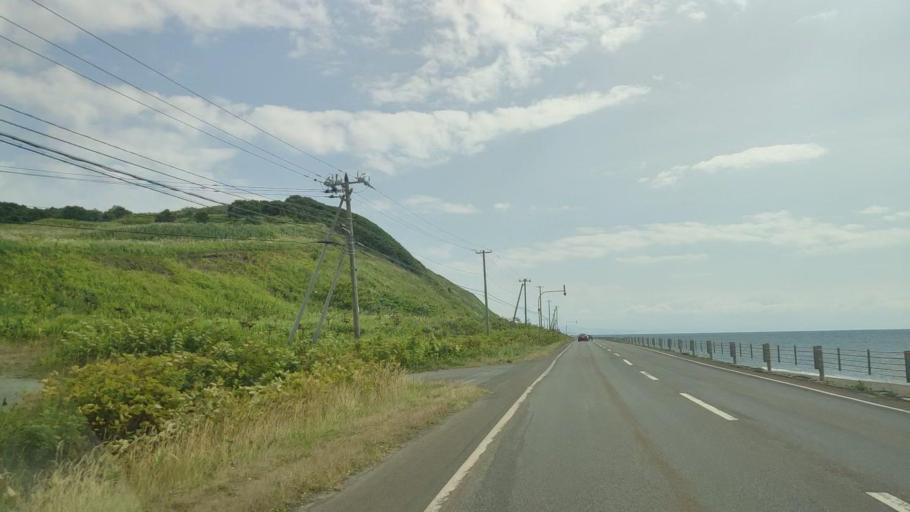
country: JP
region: Hokkaido
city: Rumoi
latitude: 44.1006
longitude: 141.6606
